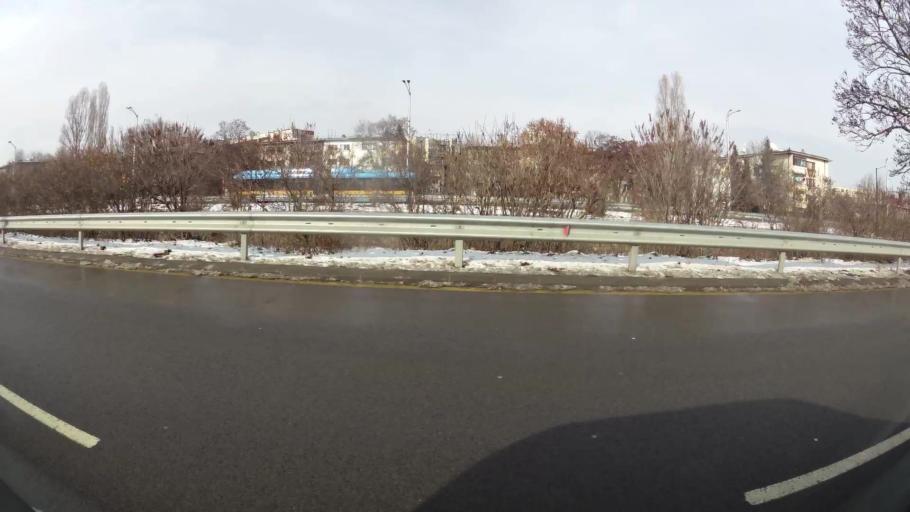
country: BG
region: Sofia-Capital
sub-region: Stolichna Obshtina
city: Sofia
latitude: 42.7048
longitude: 23.3582
